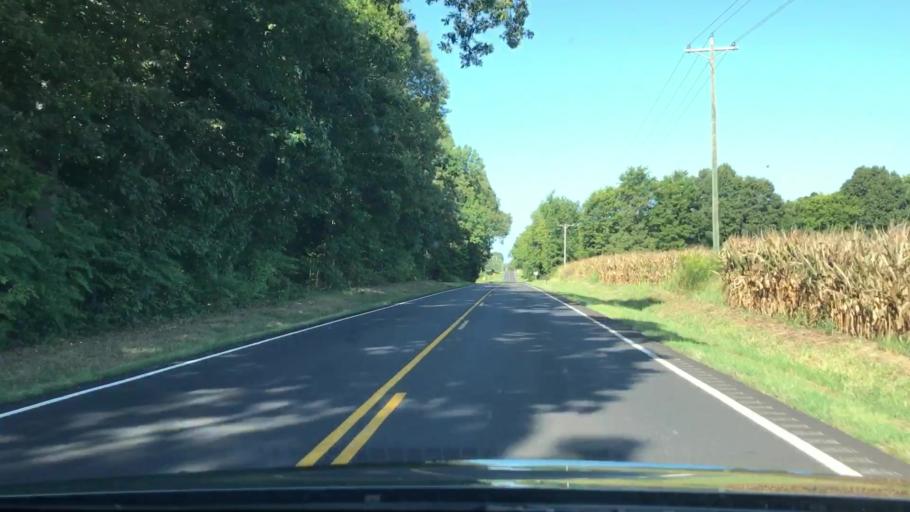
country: US
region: Kentucky
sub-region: Marshall County
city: Benton
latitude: 36.7649
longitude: -88.3721
